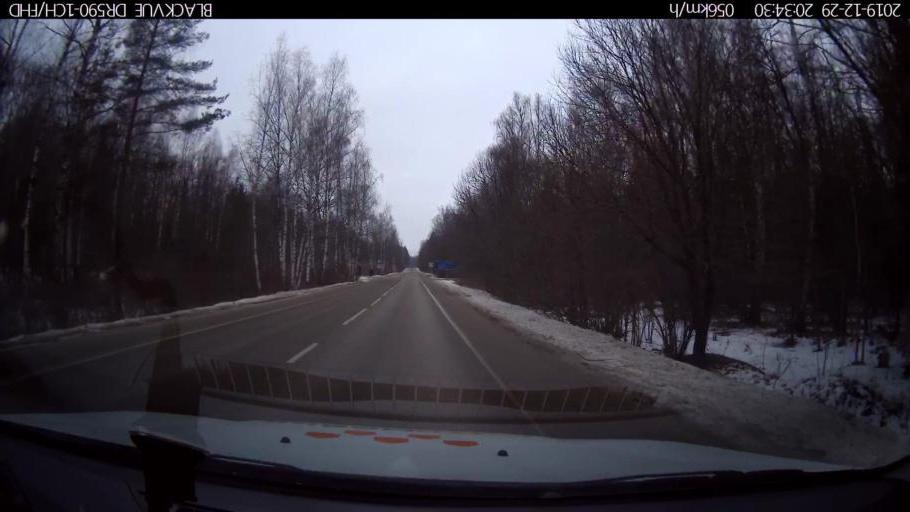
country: RU
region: Nizjnij Novgorod
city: Afonino
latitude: 56.1864
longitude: 44.0388
